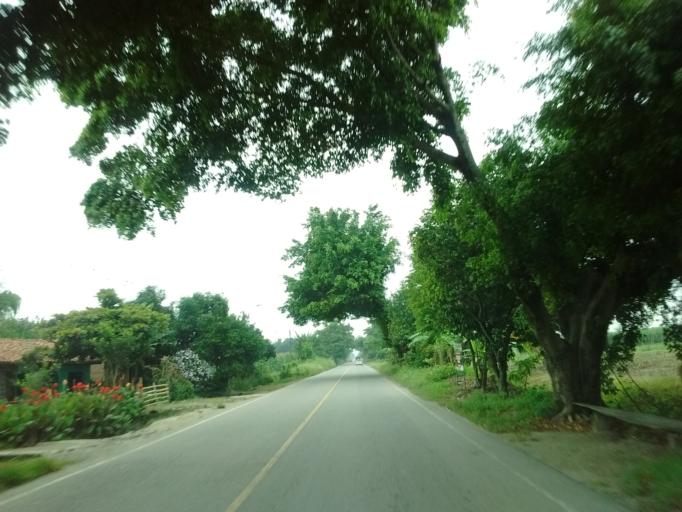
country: CO
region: Cauca
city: Padilla
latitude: 3.2248
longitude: -76.3592
